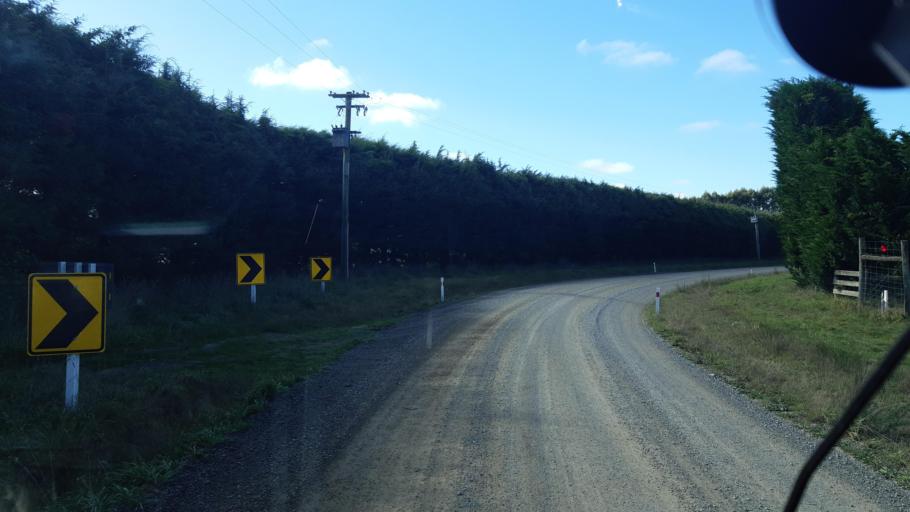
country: NZ
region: Canterbury
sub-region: Waimakariri District
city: Woodend
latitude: -43.2601
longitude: 172.4780
